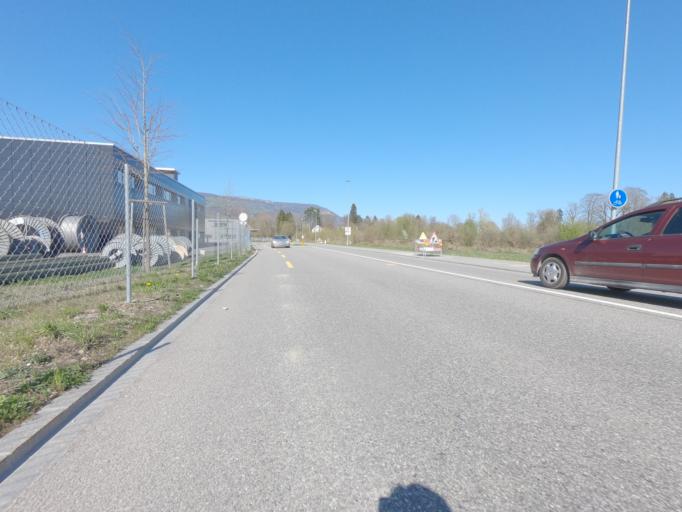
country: CH
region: Solothurn
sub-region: Bezirk Wasseramt
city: Luterbach
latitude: 47.2244
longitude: 7.5859
